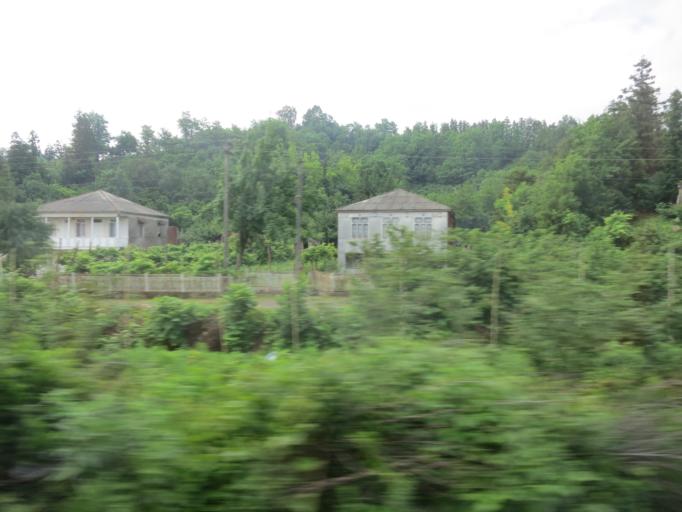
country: GE
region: Guria
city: Urek'i
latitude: 42.0651
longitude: 41.8800
